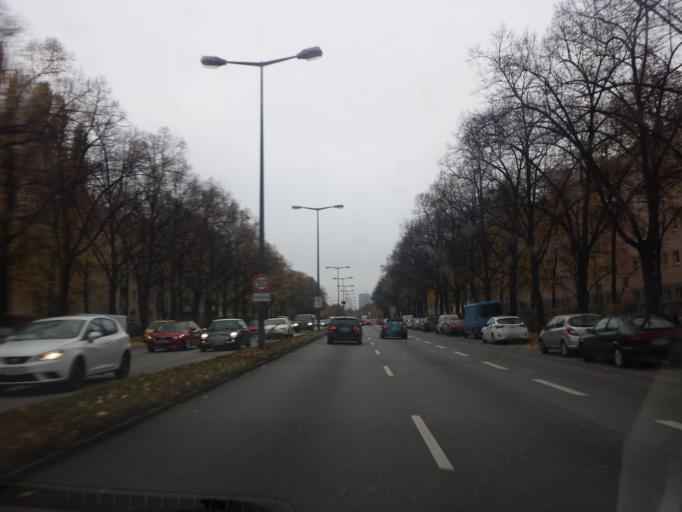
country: DE
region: Bavaria
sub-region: Upper Bavaria
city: Munich
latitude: 48.1594
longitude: 11.5375
